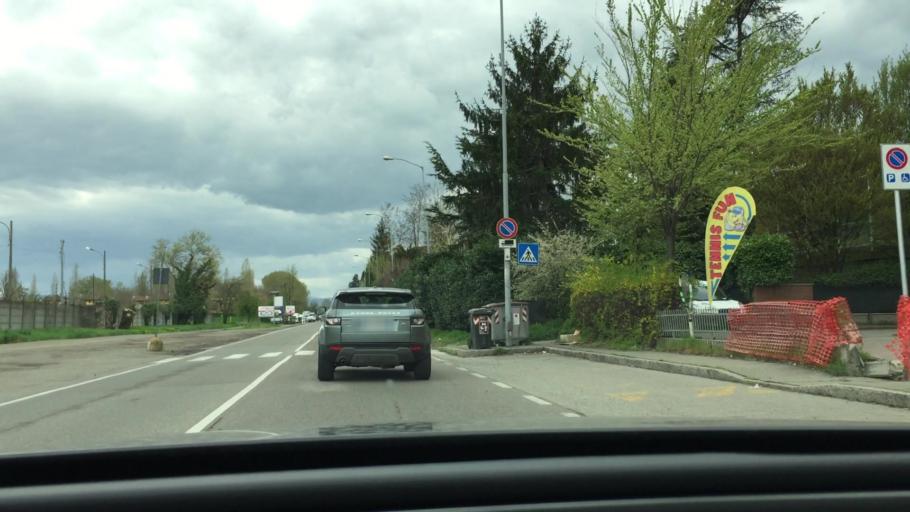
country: IT
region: Emilia-Romagna
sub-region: Provincia di Modena
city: Modena
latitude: 44.6283
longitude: 10.8972
